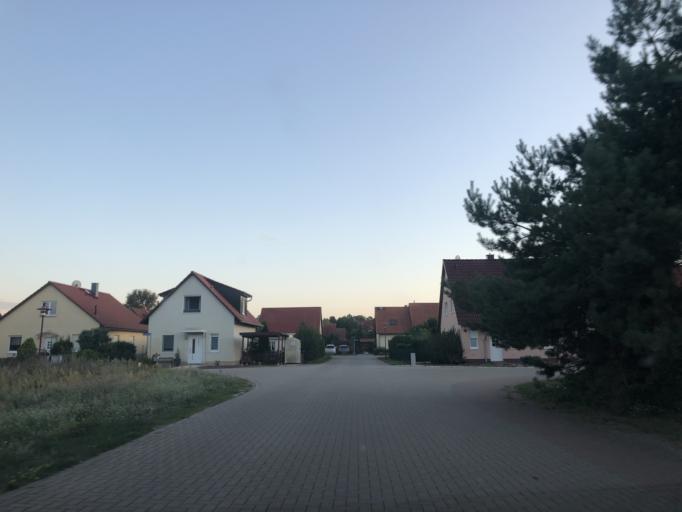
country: DE
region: Brandenburg
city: Mullrose
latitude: 52.2556
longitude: 14.4157
